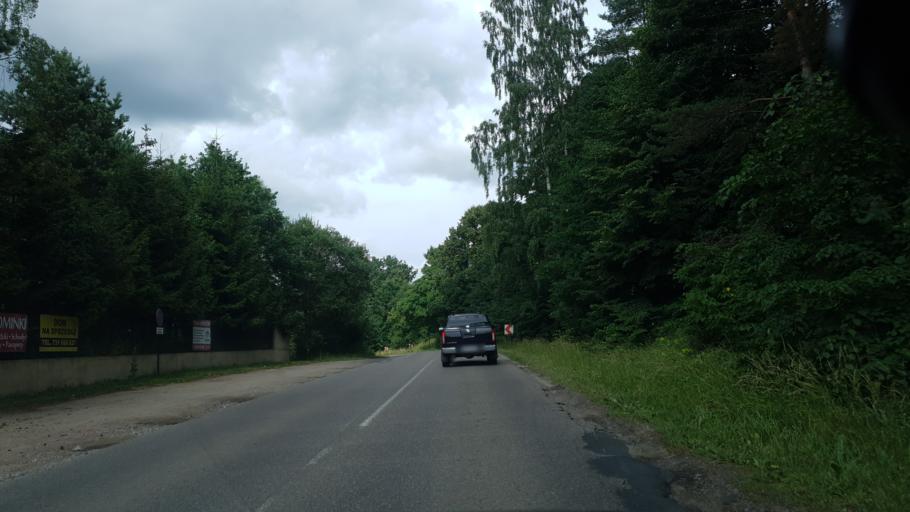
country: PL
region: Pomeranian Voivodeship
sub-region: Powiat kartuski
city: Przodkowo
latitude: 54.3639
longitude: 18.2640
